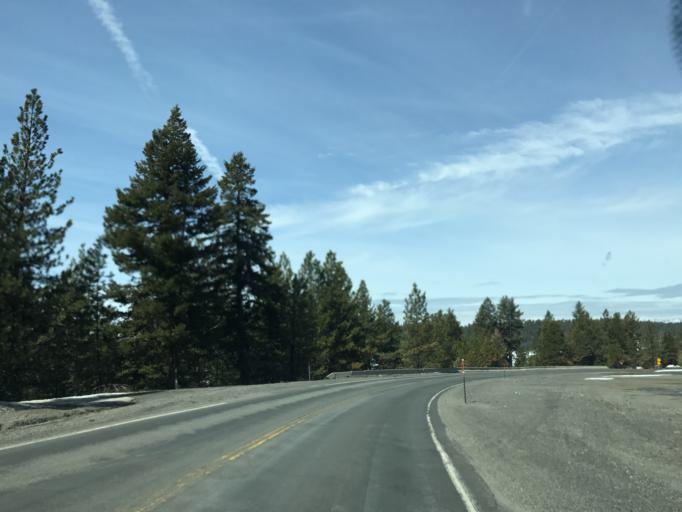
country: US
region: Idaho
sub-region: Valley County
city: McCall
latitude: 44.9306
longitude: -116.1633
